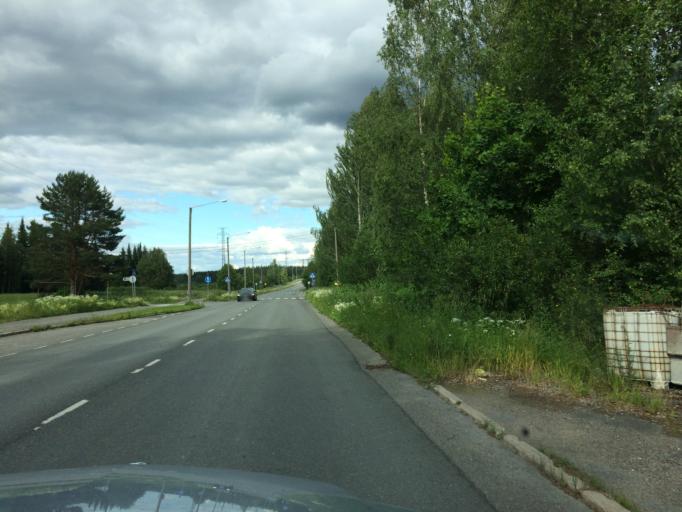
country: FI
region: Haeme
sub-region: Haemeenlinna
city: Parola
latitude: 61.0176
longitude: 24.4019
